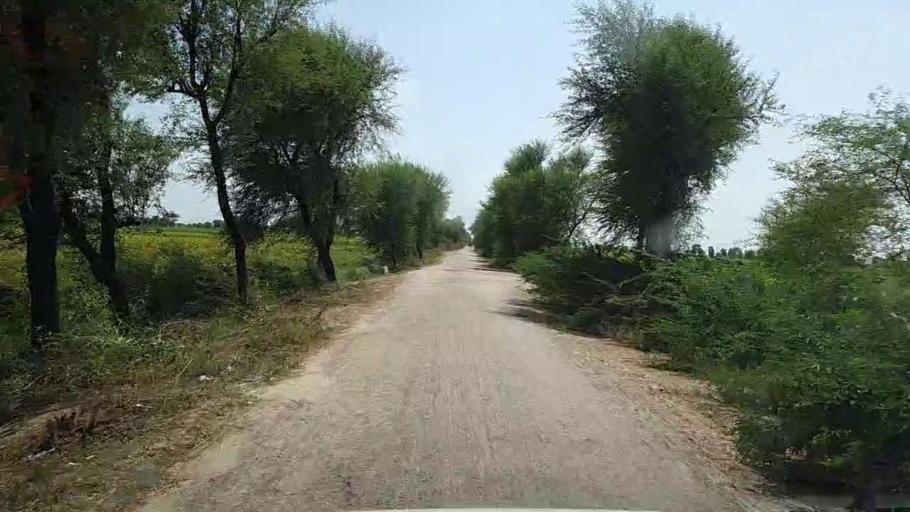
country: PK
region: Sindh
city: Kario
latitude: 24.6508
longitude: 68.5640
